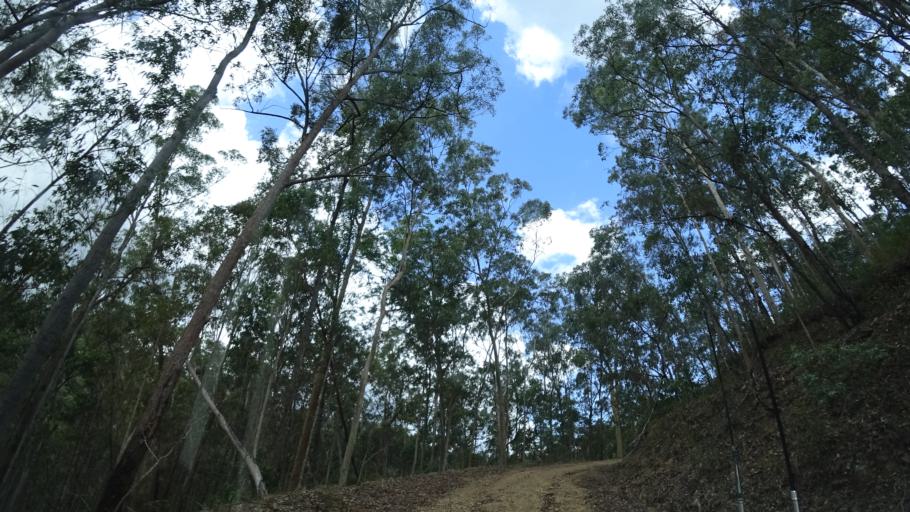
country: AU
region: Queensland
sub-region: Moreton Bay
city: Highvale
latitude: -27.3427
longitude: 152.7297
